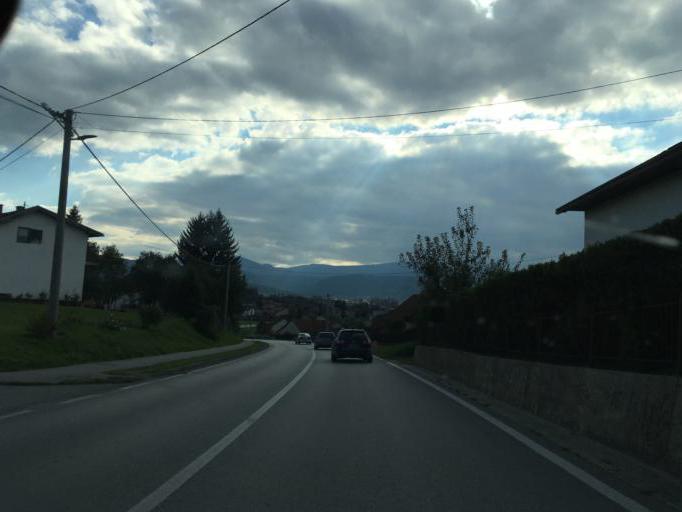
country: BA
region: Federation of Bosnia and Herzegovina
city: Bugojno
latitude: 44.0618
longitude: 17.4669
